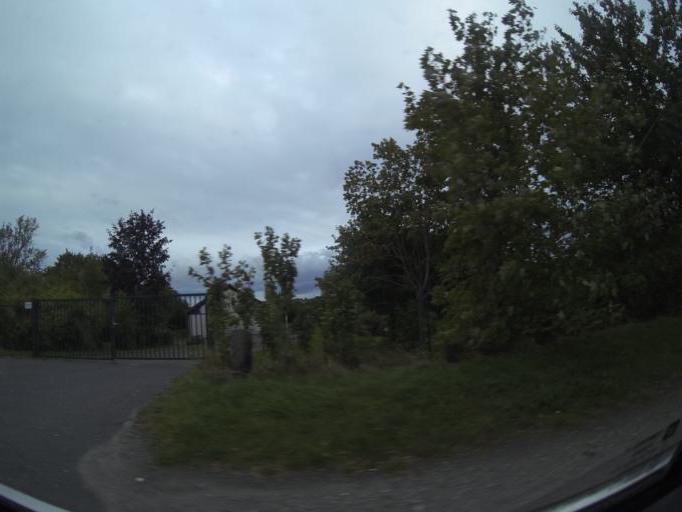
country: DE
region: Thuringia
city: Nobdenitz
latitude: 50.8793
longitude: 12.2818
